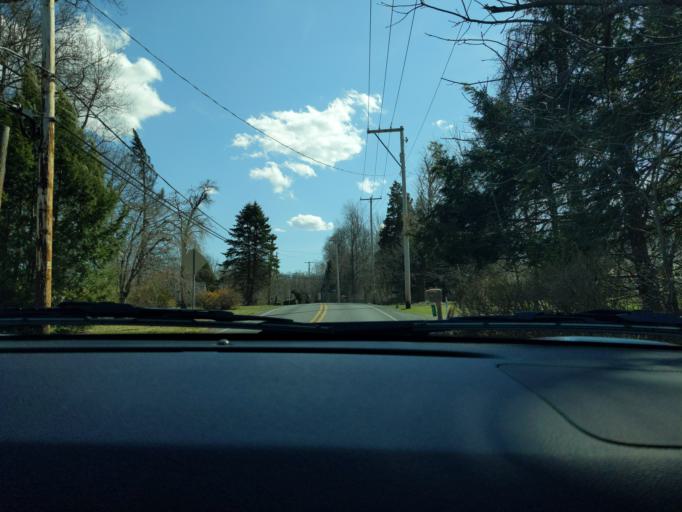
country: US
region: Pennsylvania
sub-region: Bucks County
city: Richlandtown
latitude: 40.4677
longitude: -75.2735
